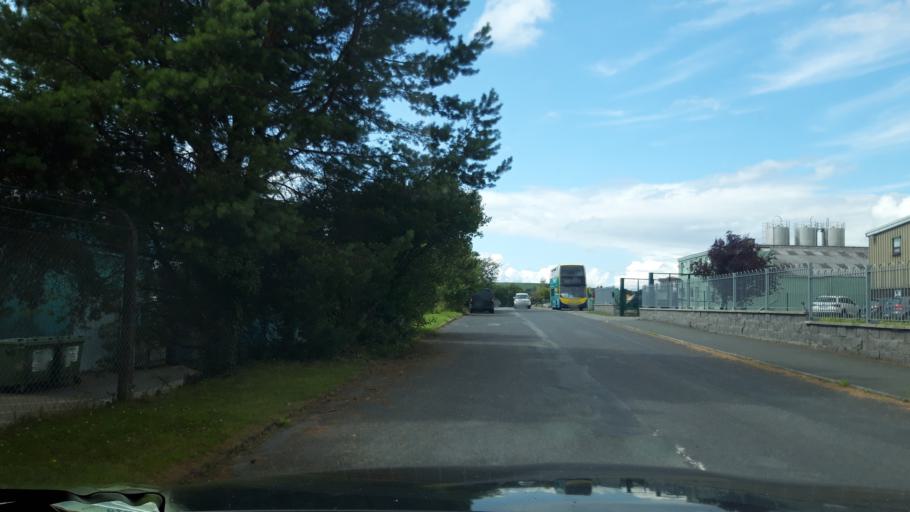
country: IE
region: Leinster
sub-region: Wicklow
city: Blessington
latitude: 53.1647
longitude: -6.5380
